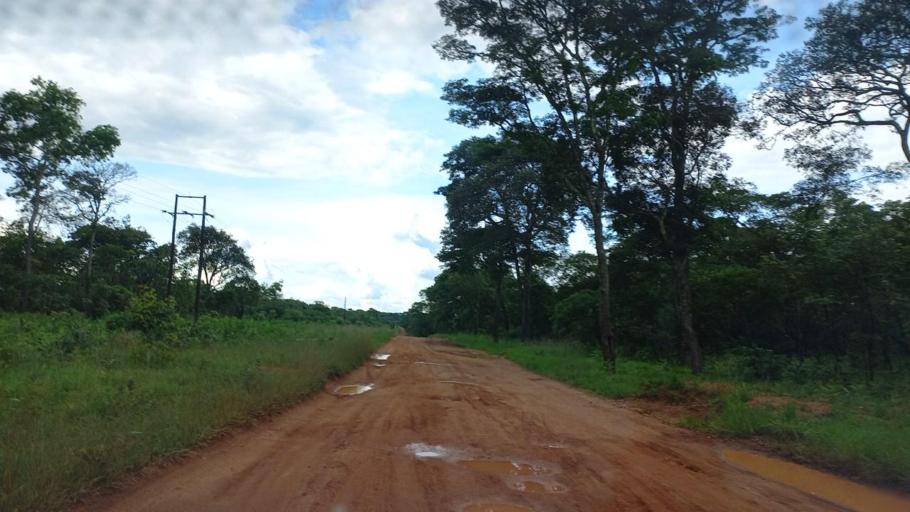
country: ZM
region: North-Western
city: Mwinilunga
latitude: -11.7916
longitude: 24.3724
